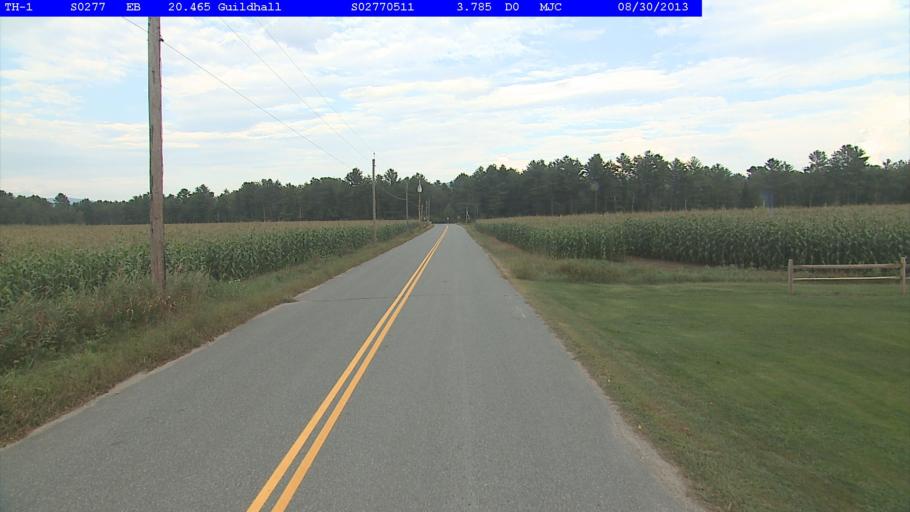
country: US
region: Vermont
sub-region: Essex County
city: Guildhall
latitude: 44.5586
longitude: -71.6029
